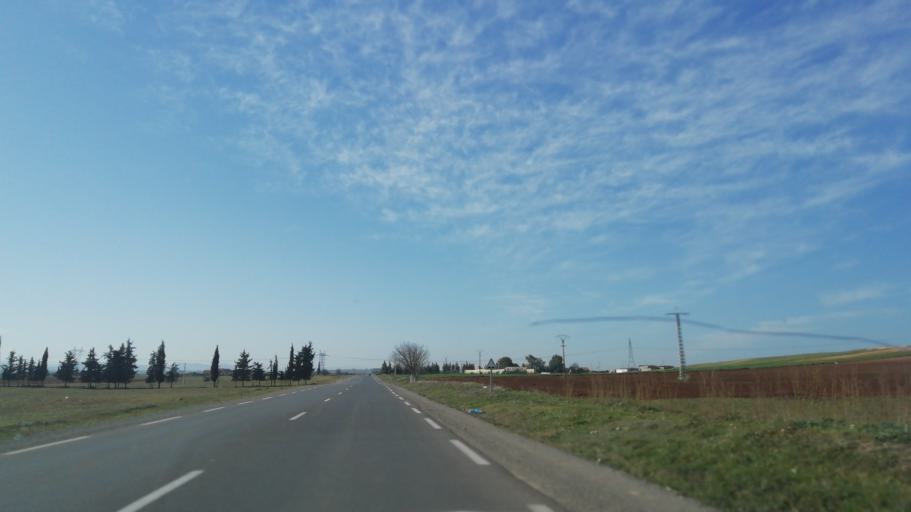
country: DZ
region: Tlemcen
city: Ouled Mimoun
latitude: 35.0451
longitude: -0.8398
